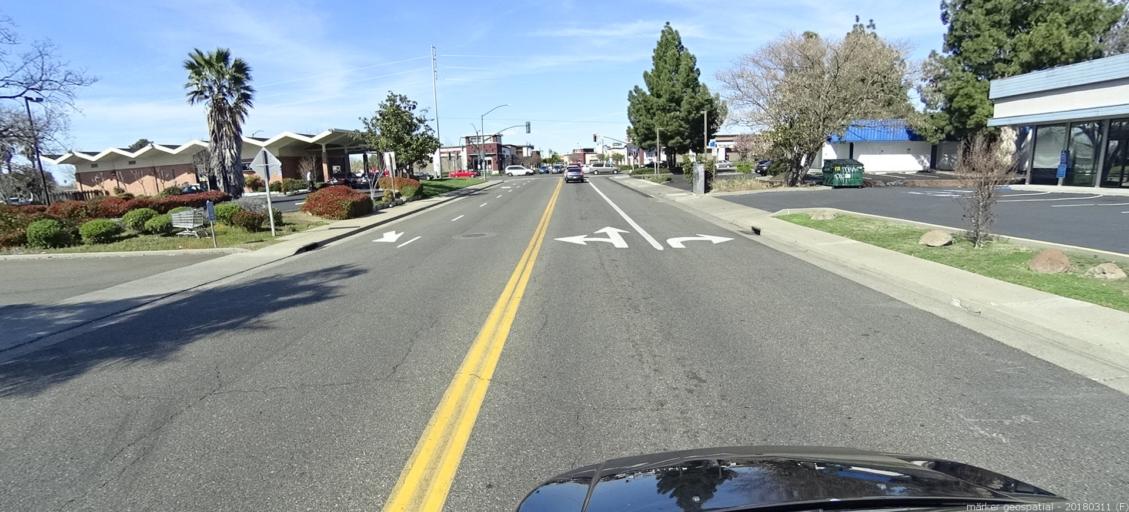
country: US
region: California
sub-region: Sacramento County
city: Parkway
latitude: 38.4952
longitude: -121.4344
